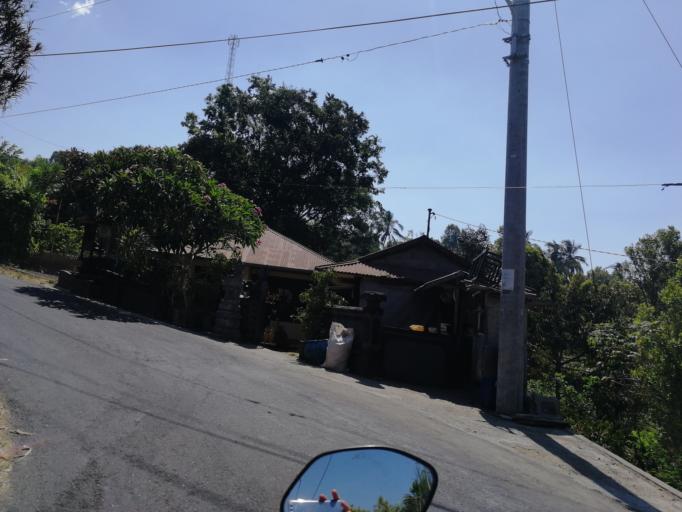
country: ID
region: Bali
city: Banjar Kedisan
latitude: -8.1539
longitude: 115.3078
